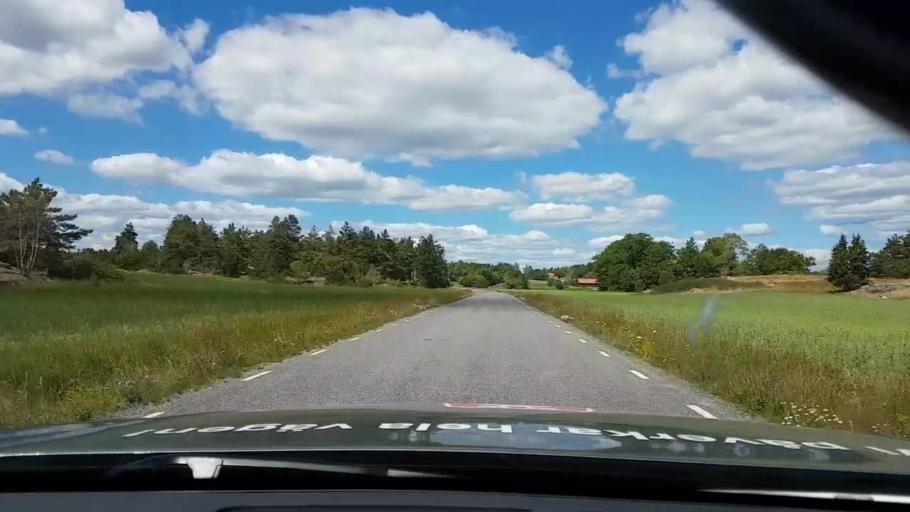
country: SE
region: Kalmar
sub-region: Vasterviks Kommun
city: Forserum
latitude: 58.0042
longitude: 16.5876
